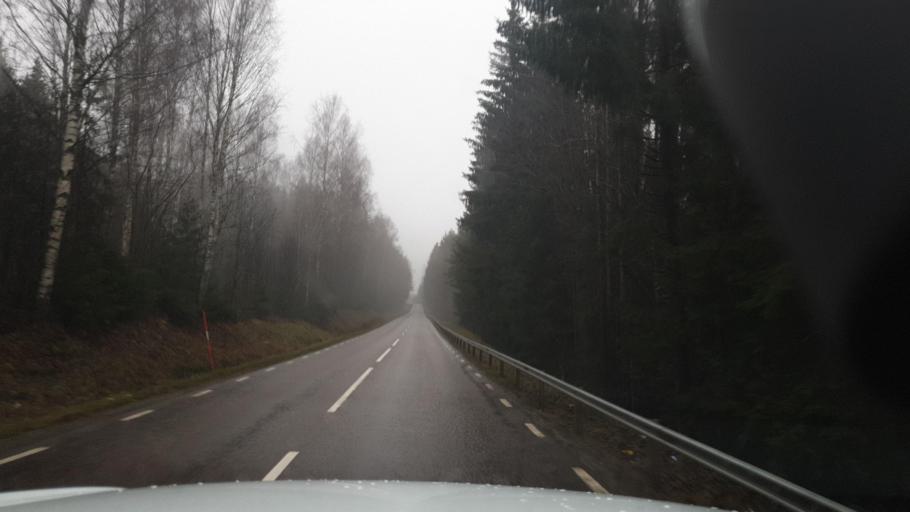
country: SE
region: Vaermland
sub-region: Arvika Kommun
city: Arvika
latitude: 59.6275
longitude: 12.8880
